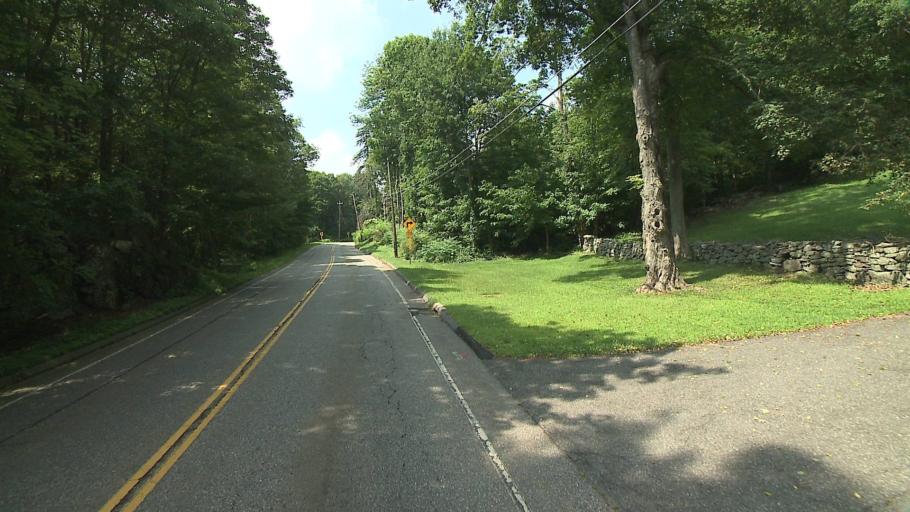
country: US
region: Connecticut
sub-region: Litchfield County
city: Bethlehem Village
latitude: 41.6744
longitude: -73.1551
